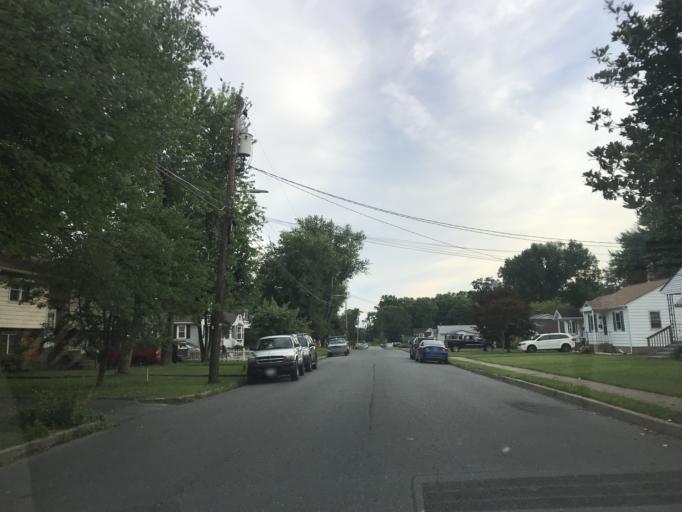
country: US
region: Maryland
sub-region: Harford County
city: Aberdeen
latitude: 39.5045
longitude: -76.1689
